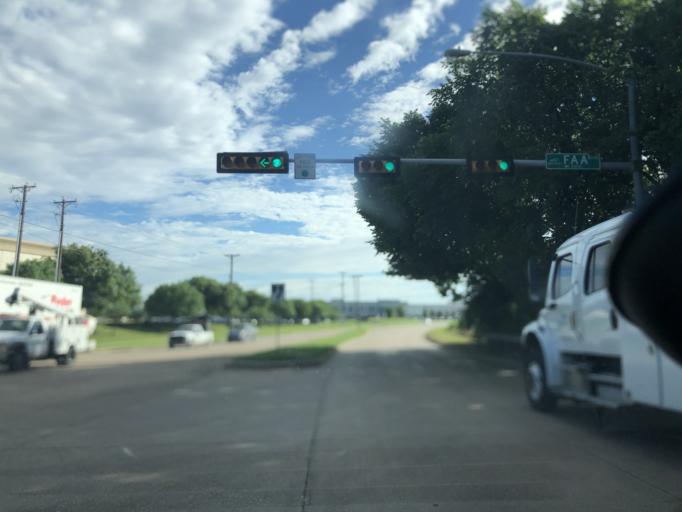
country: US
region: Texas
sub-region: Tarrant County
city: Euless
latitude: 32.8273
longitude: -97.0300
